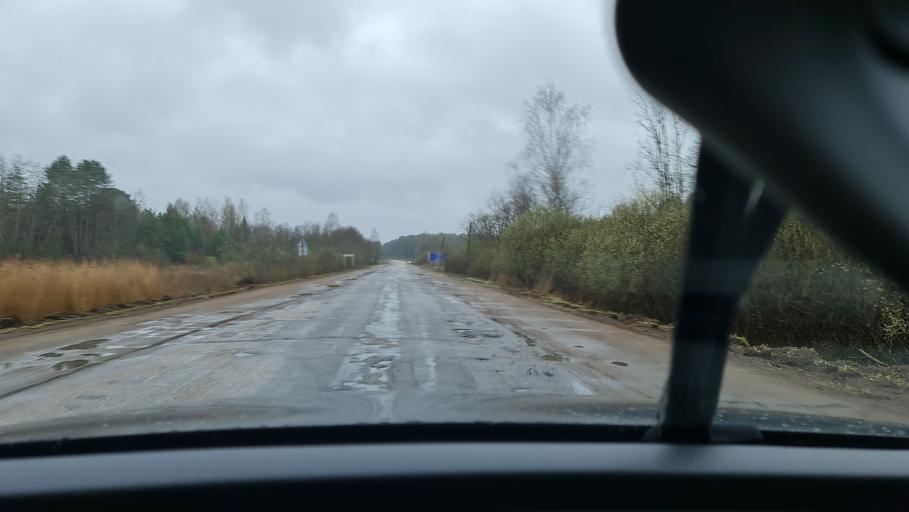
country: RU
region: Novgorod
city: Valday
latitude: 58.0381
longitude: 32.9358
